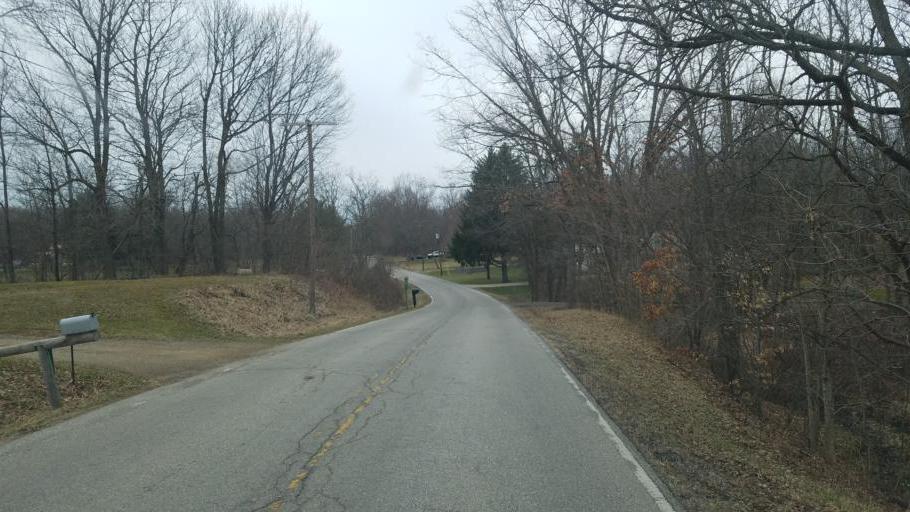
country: US
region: Ohio
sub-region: Richland County
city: Ontario
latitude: 40.8117
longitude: -82.5560
